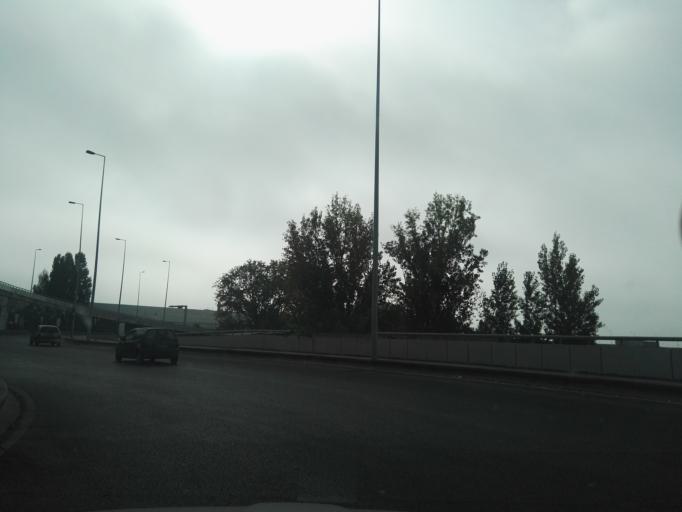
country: PT
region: Lisbon
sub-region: Loures
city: Moscavide
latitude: 38.7539
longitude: -9.0971
